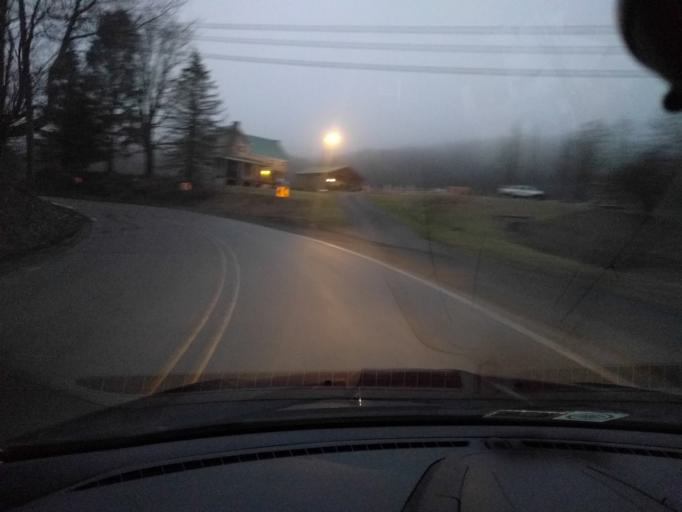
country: US
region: West Virginia
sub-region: Greenbrier County
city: Rainelle
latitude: 37.9690
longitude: -80.8070
